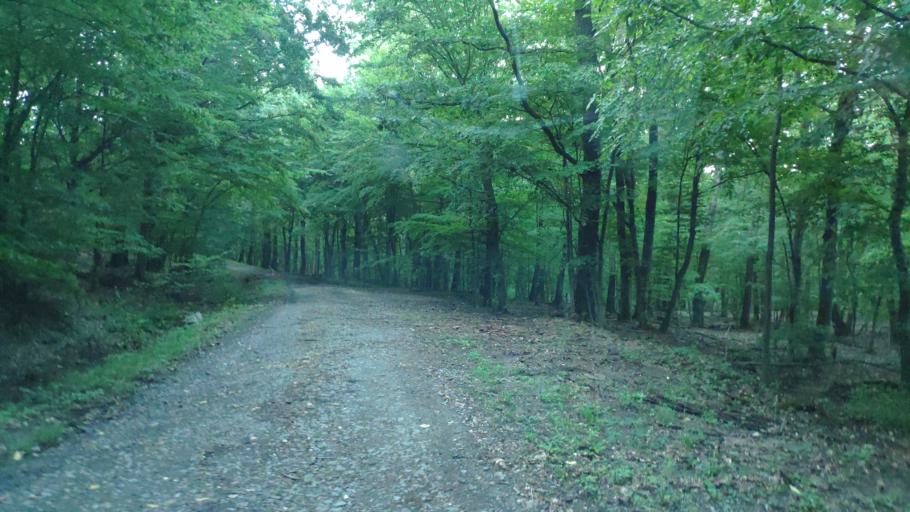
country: SK
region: Kosicky
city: Secovce
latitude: 48.5830
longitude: 21.5340
